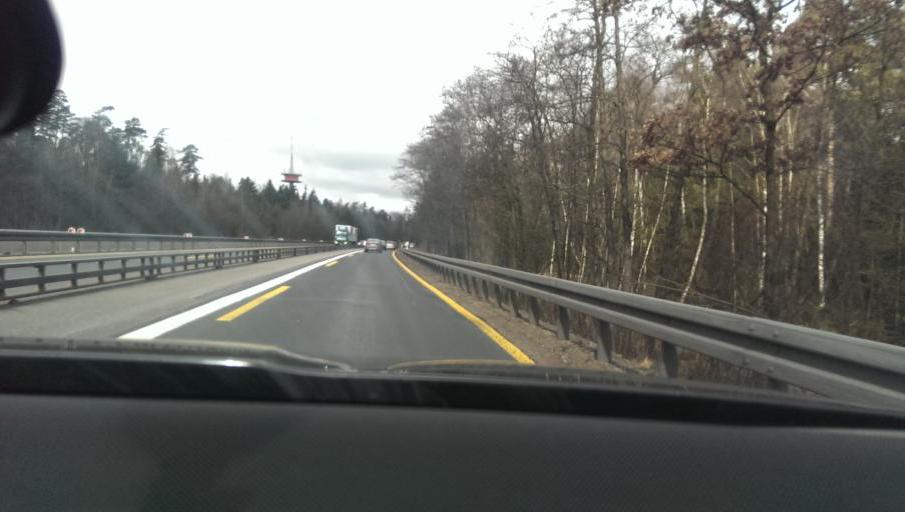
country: DE
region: Hesse
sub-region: Regierungsbezirk Kassel
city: Fulda
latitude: 50.5978
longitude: 9.6827
